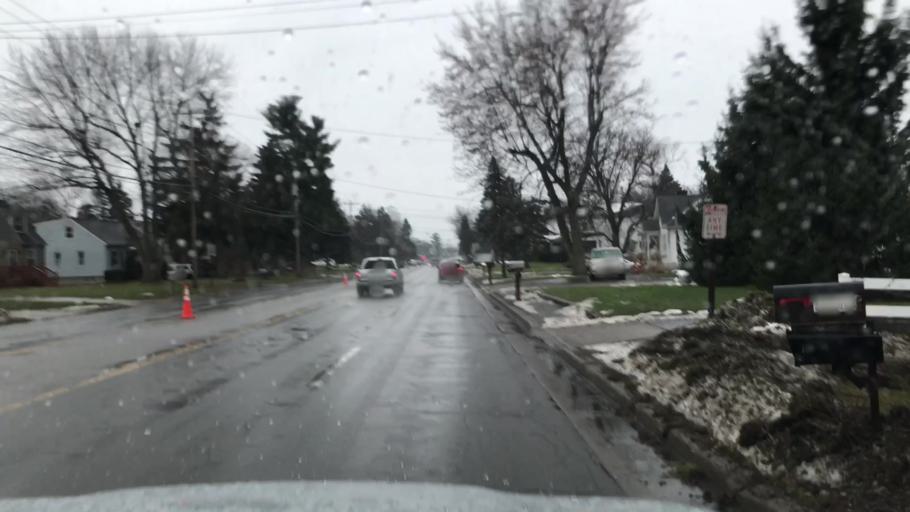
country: US
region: New York
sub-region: Erie County
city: Blasdell
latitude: 42.7873
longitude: -78.7915
